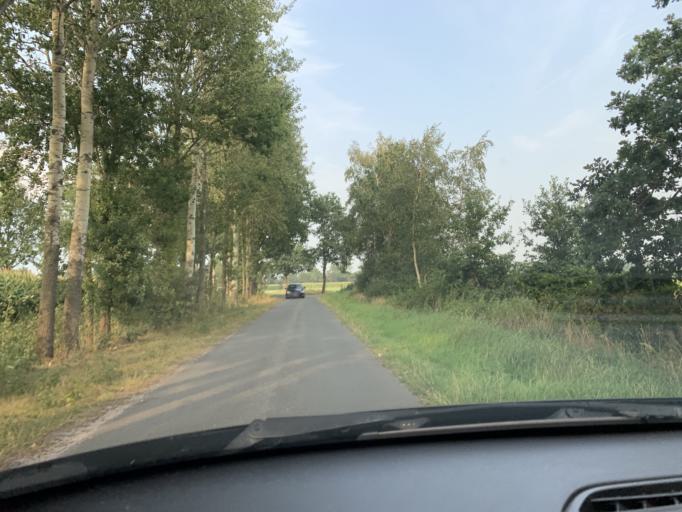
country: DE
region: Lower Saxony
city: Apen
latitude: 53.2429
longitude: 7.8281
